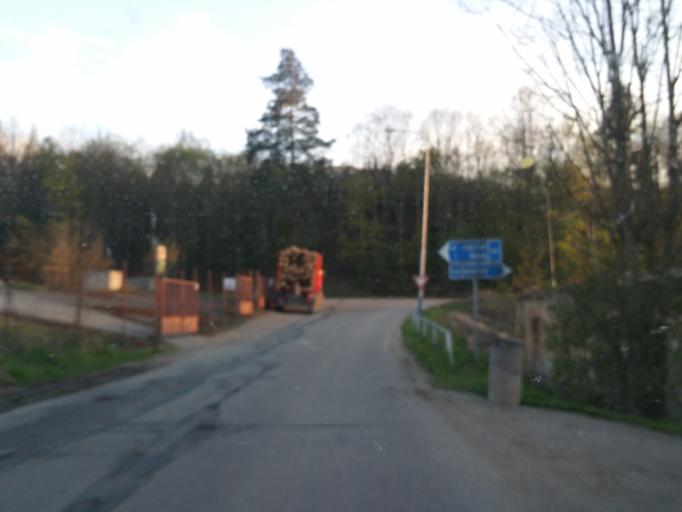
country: CZ
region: South Moravian
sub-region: Okres Blansko
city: Boskovice
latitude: 49.4825
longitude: 16.6873
